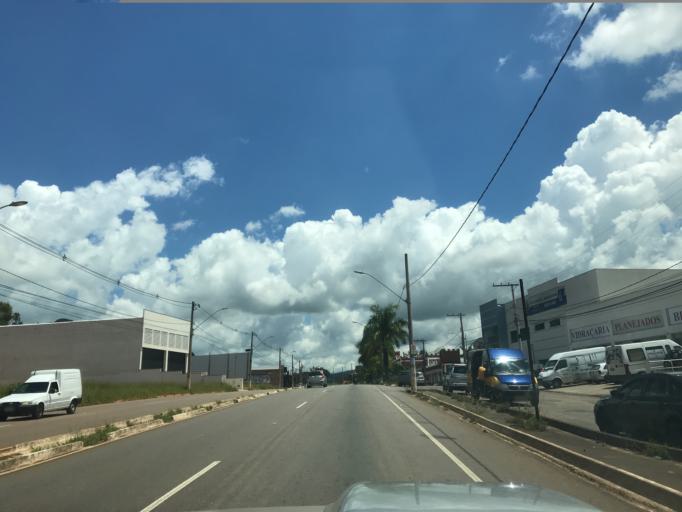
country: BR
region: Minas Gerais
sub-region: Tres Coracoes
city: Tres Coracoes
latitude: -21.6708
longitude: -45.2728
